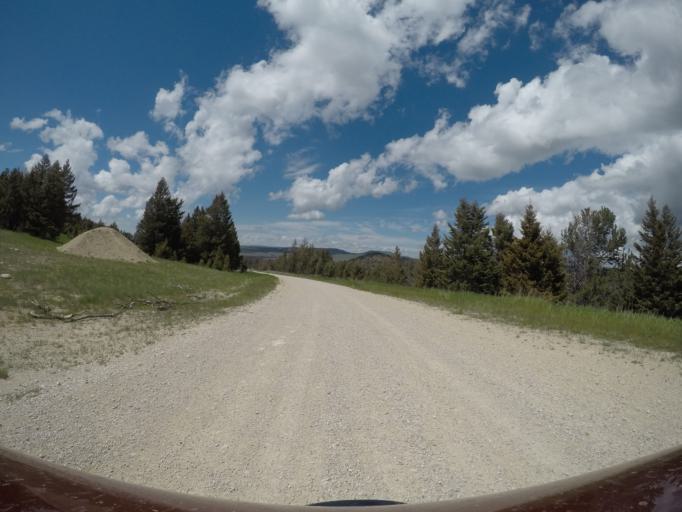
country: US
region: Wyoming
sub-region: Big Horn County
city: Lovell
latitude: 45.1947
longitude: -108.4833
